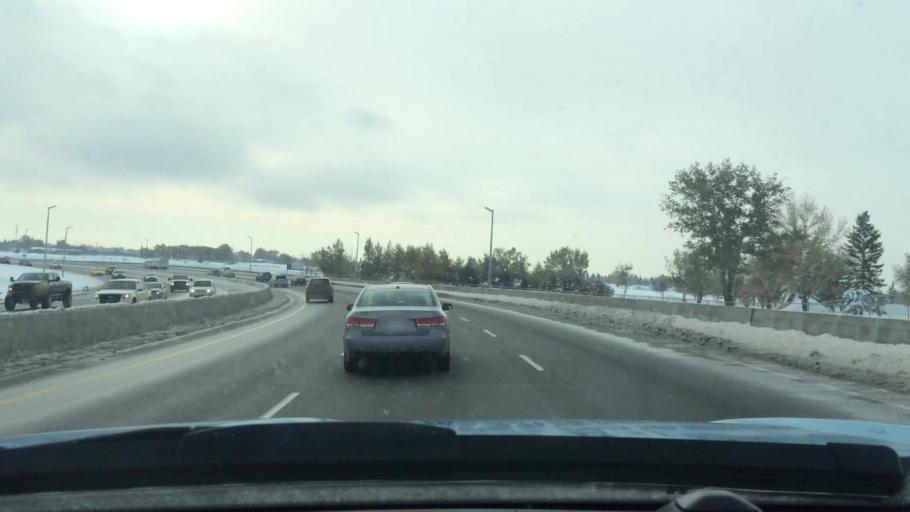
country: CA
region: Alberta
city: Calgary
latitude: 51.0939
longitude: -114.0261
